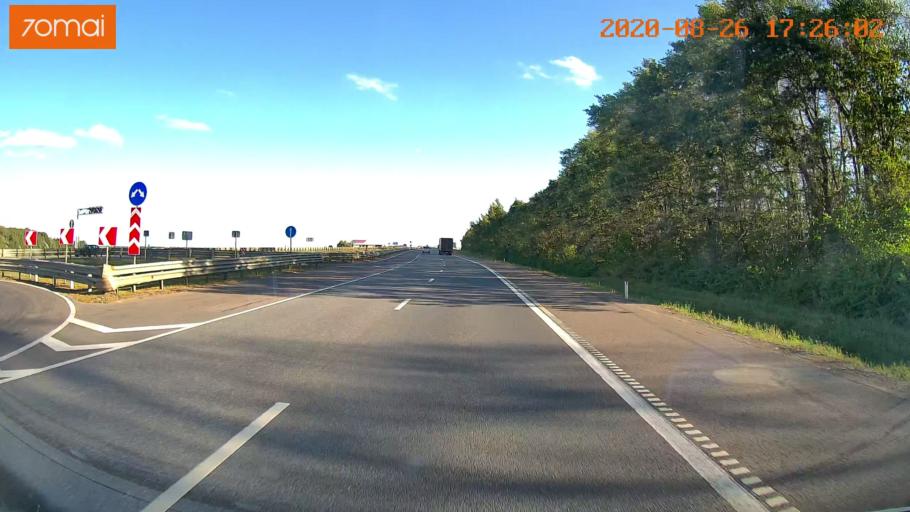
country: RU
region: Tula
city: Volovo
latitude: 53.4923
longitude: 38.1137
